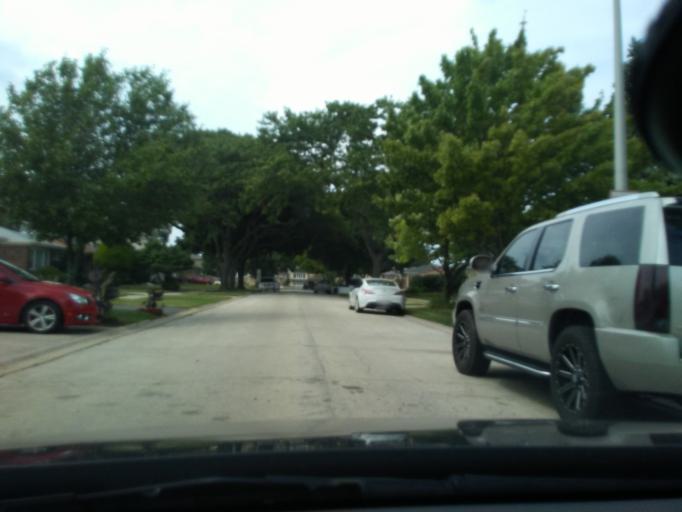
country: US
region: Illinois
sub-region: Cook County
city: Norridge
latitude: 41.9689
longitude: -87.8404
